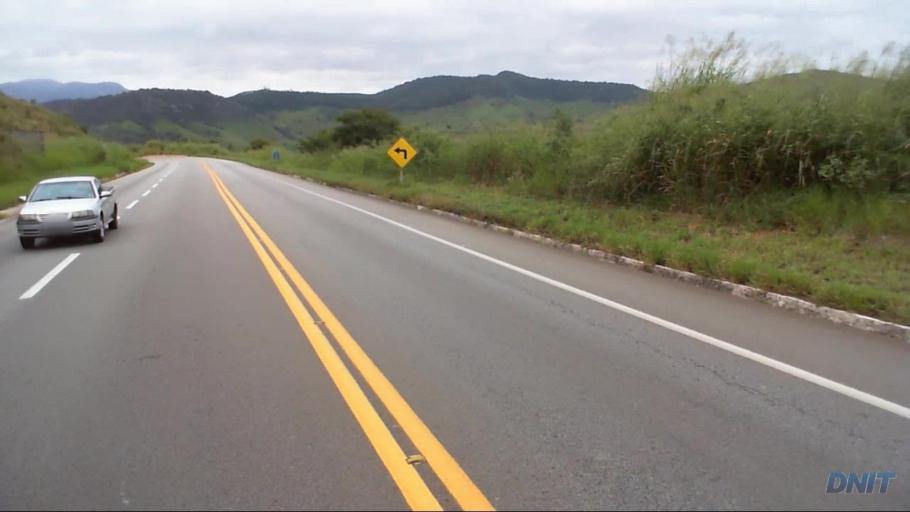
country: BR
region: Minas Gerais
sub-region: Nova Era
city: Nova Era
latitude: -19.8029
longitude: -43.0579
